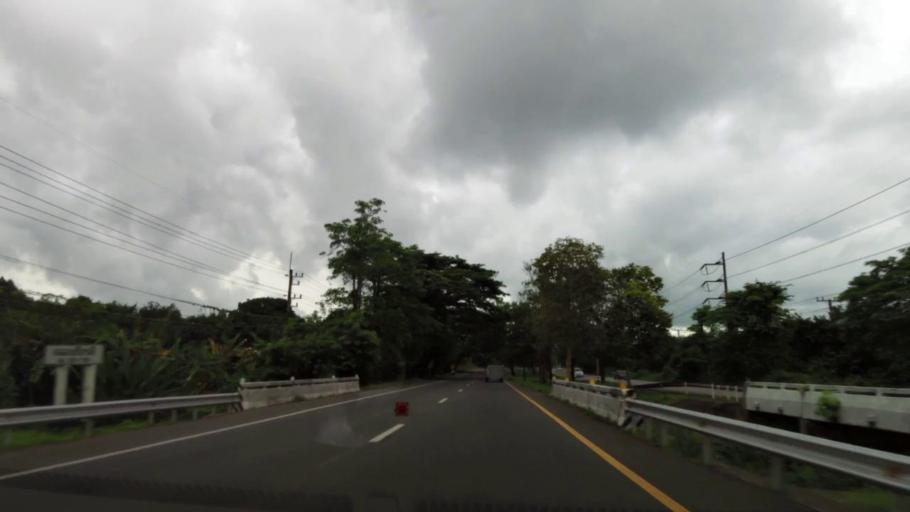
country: TH
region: Chanthaburi
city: Tha Mai
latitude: 12.6738
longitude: 102.0054
